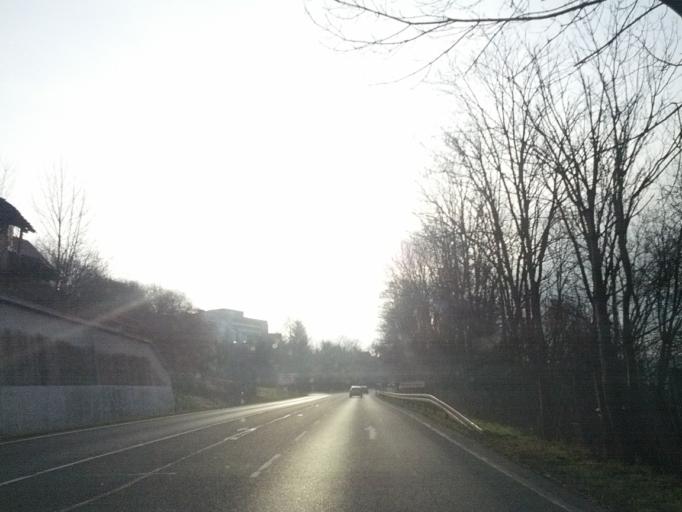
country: DE
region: Thuringia
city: Utendorf
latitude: 50.5968
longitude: 10.4121
